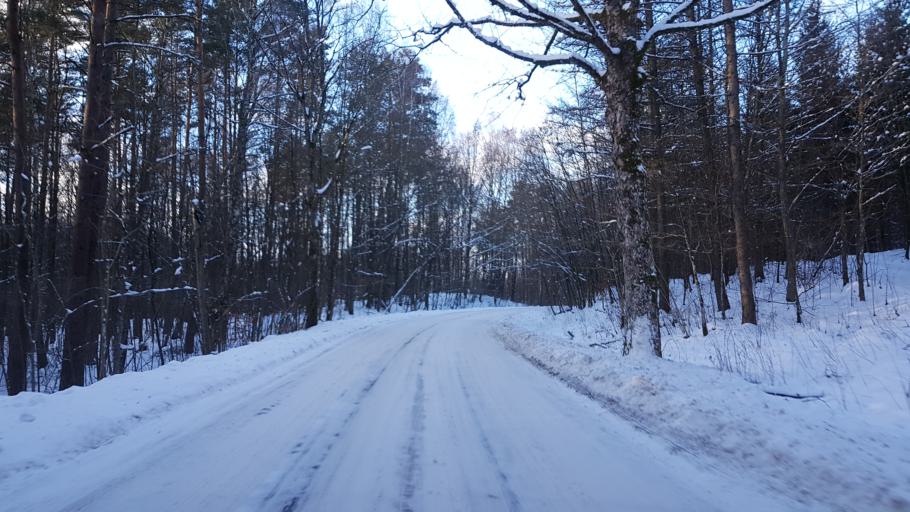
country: PL
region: West Pomeranian Voivodeship
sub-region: Powiat koszalinski
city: Bobolice
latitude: 53.9693
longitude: 16.7022
